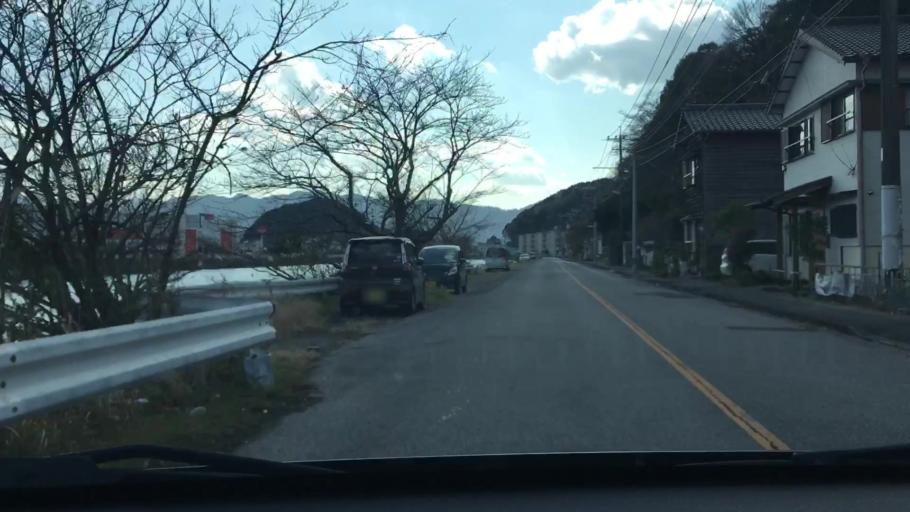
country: JP
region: Oita
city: Saiki
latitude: 32.9678
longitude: 131.9144
